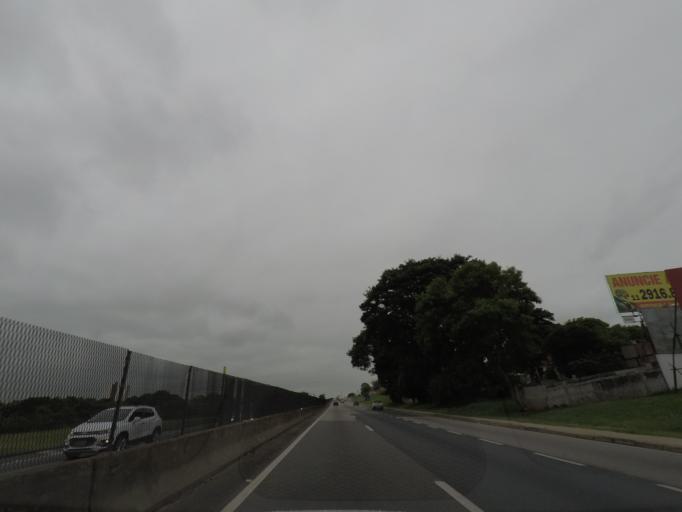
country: BR
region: Sao Paulo
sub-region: Taubate
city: Taubate
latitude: -23.0209
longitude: -45.5343
